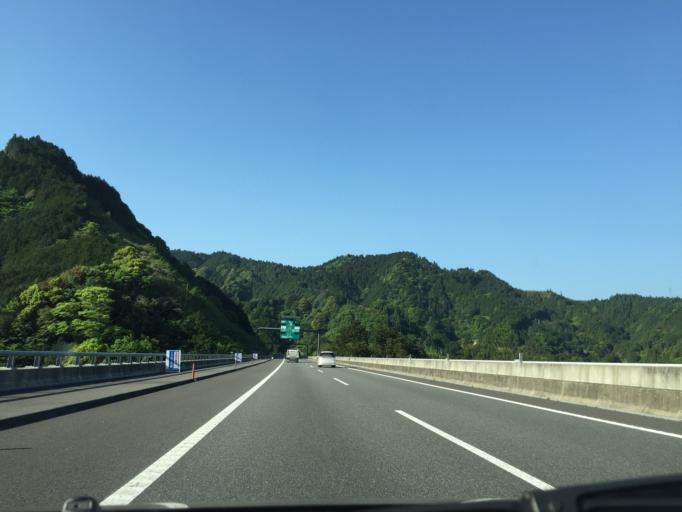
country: JP
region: Shizuoka
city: Shizuoka-shi
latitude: 35.1061
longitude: 138.4827
